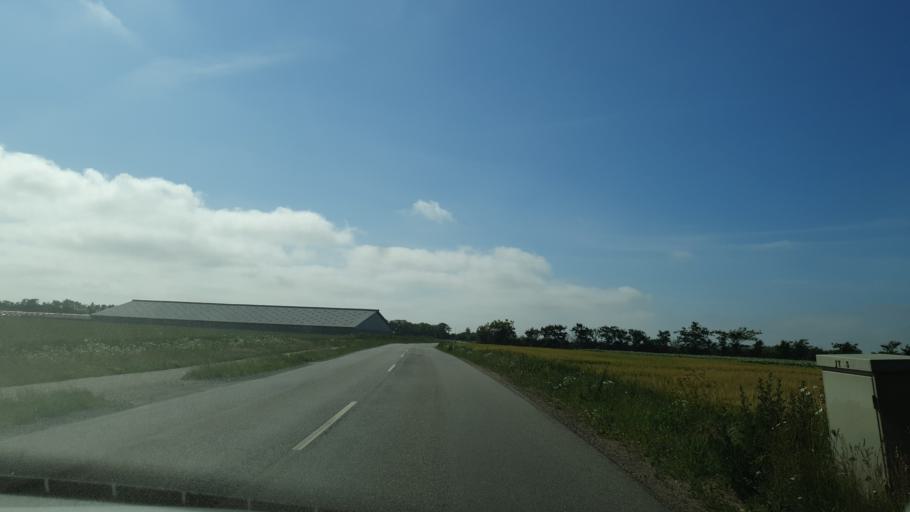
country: DK
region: Central Jutland
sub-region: Ringkobing-Skjern Kommune
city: Ringkobing
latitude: 56.0299
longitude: 8.3484
